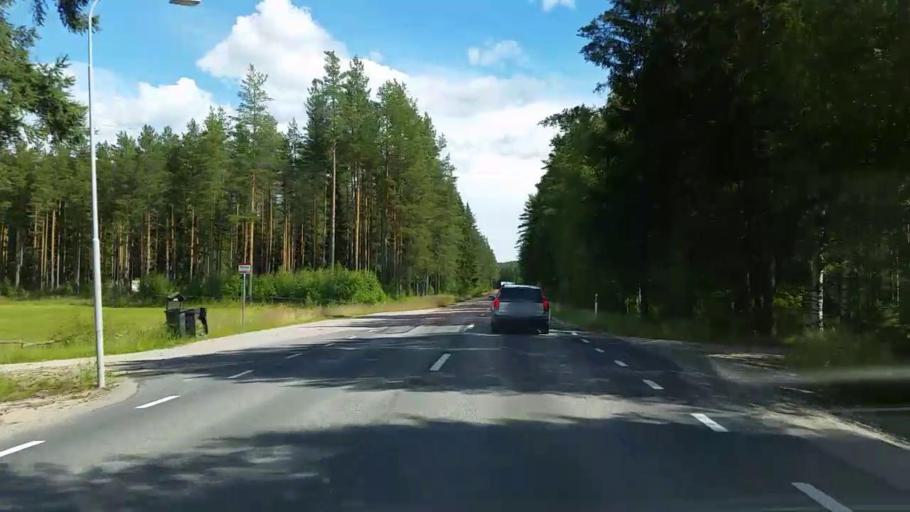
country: SE
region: Gaevleborg
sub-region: Ovanakers Kommun
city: Edsbyn
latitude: 61.3459
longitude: 15.6523
